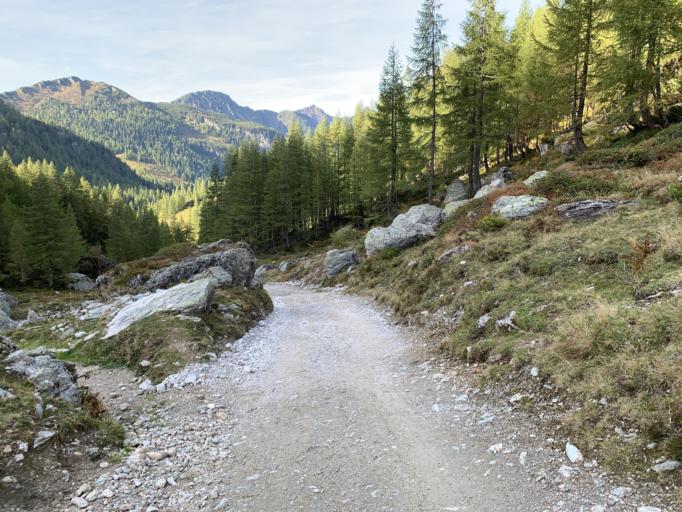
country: AT
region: Salzburg
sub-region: Politischer Bezirk Tamsweg
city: Tweng
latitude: 47.2934
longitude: 13.6297
